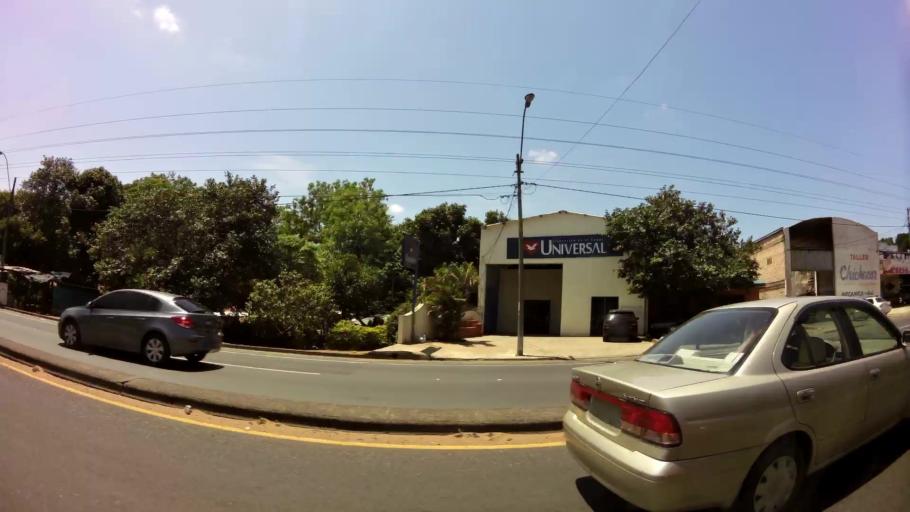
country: PY
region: Central
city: Nemby
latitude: -25.4009
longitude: -57.5436
